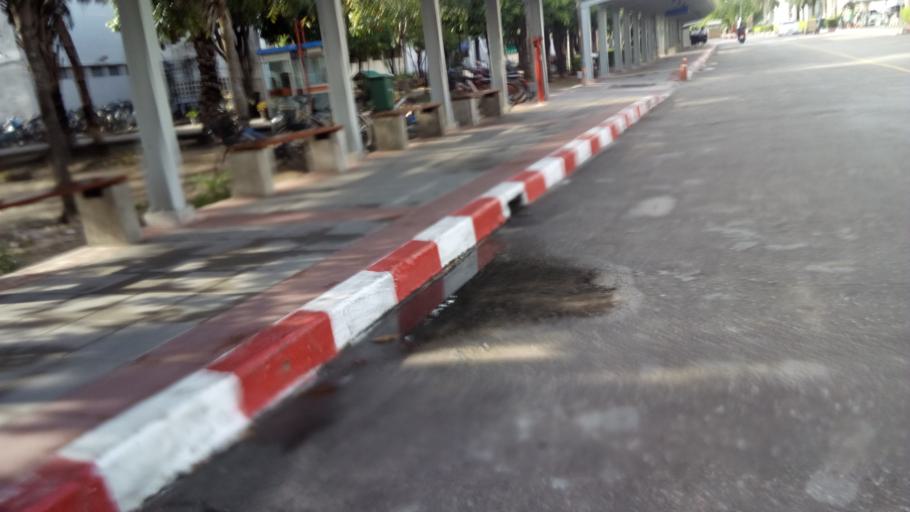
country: TH
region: Nakhon Nayok
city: Ongkharak
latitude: 14.1053
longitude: 100.9886
